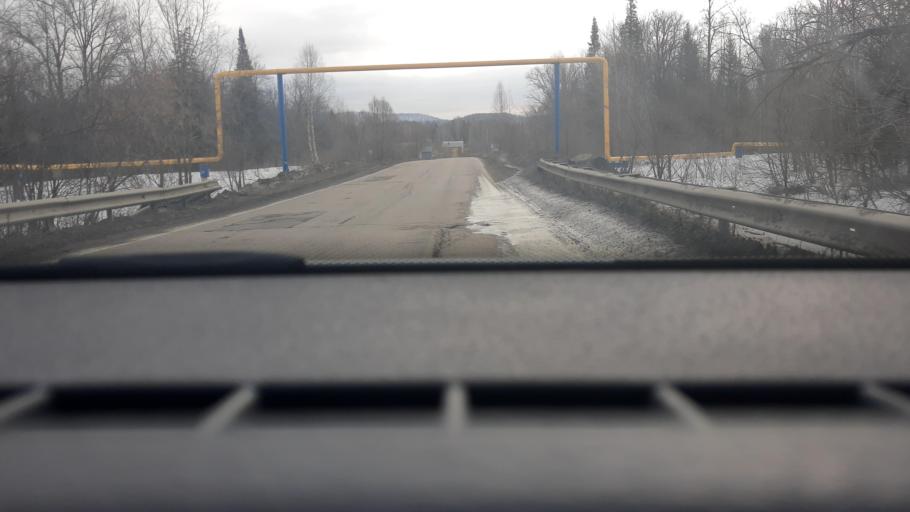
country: RU
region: Chelyabinsk
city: Asha
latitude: 54.9721
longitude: 57.2817
